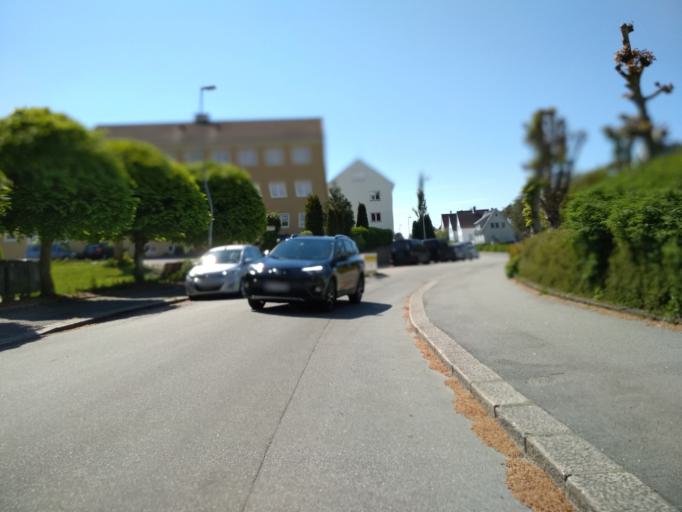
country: NO
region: Rogaland
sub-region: Stavanger
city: Stavanger
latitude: 58.9709
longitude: 5.7142
